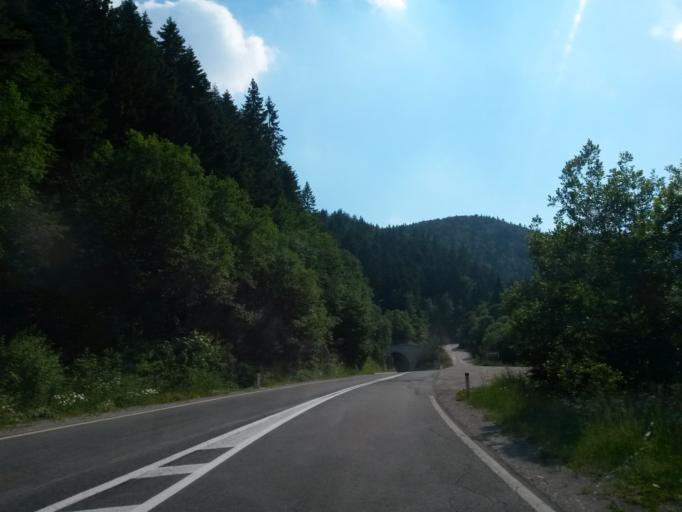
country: BA
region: Federation of Bosnia and Herzegovina
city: Bugojno
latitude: 44.0168
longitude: 17.2892
